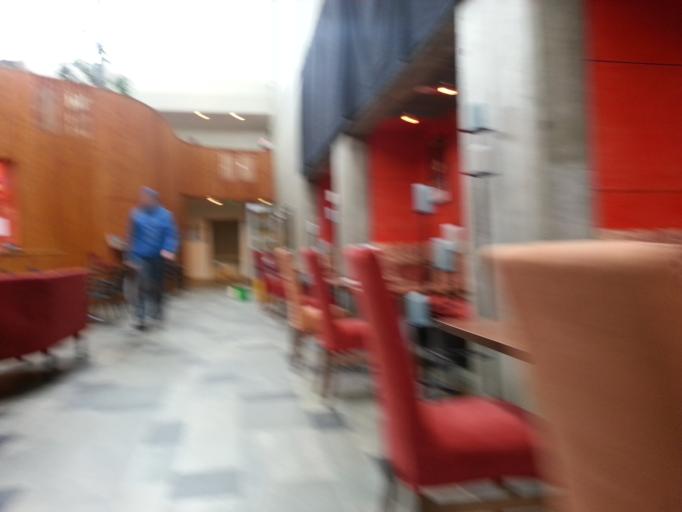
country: NO
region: Sor-Trondelag
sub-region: Oppdal
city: Oppdal
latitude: 62.5960
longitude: 9.6879
